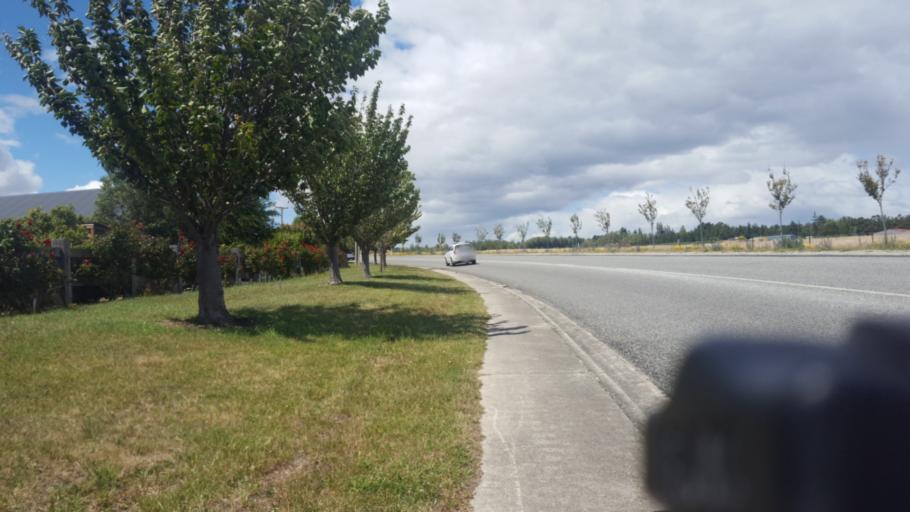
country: NZ
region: Otago
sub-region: Queenstown-Lakes District
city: Wanaka
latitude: -45.1985
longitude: 169.3326
